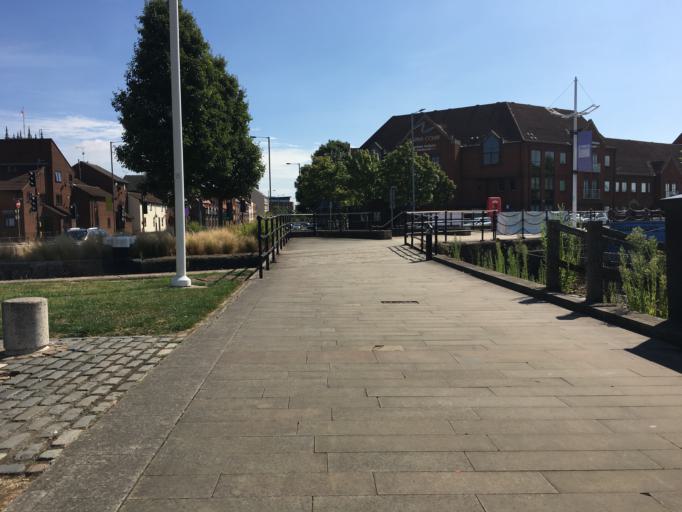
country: GB
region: England
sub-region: City of Kingston upon Hull
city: Hull
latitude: 53.7408
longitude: -0.3381
